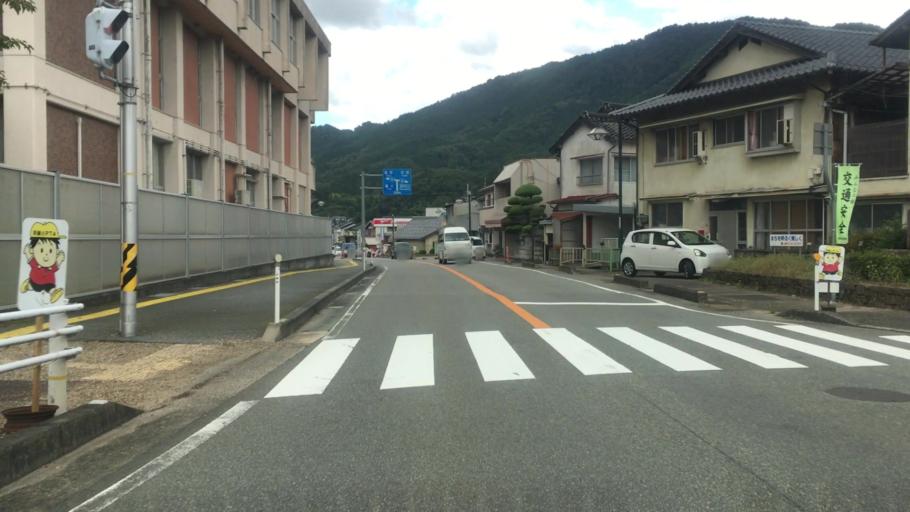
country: JP
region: Hyogo
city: Toyooka
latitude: 35.3151
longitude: 134.8834
